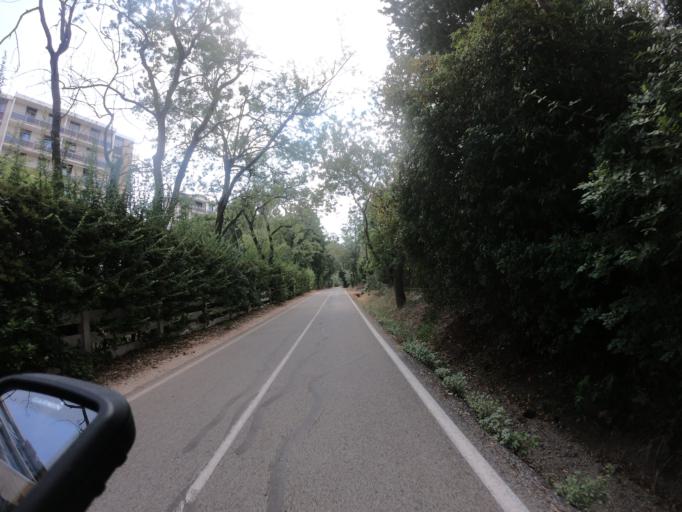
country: FR
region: Provence-Alpes-Cote d'Azur
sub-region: Departement du Var
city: La Valette-du-Var
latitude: 43.1175
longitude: 5.9718
